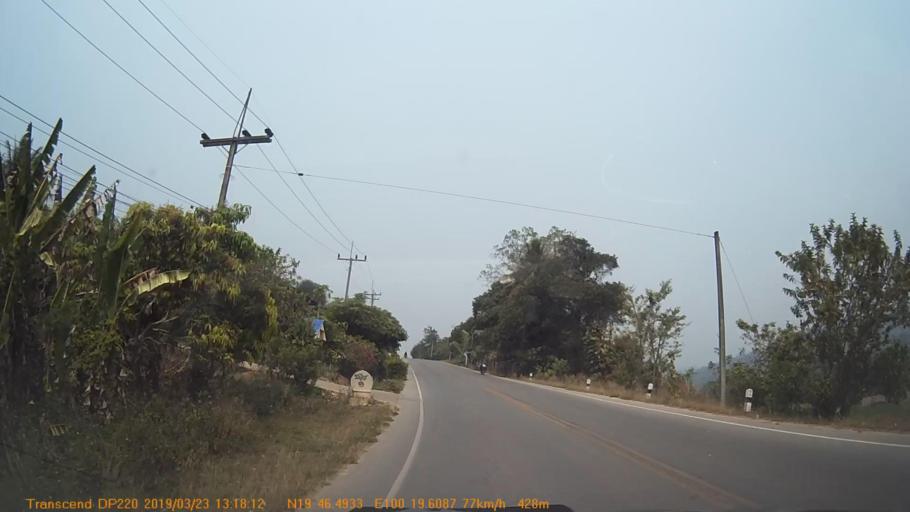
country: TH
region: Chiang Rai
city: Khun Tan
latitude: 19.7751
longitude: 100.3270
